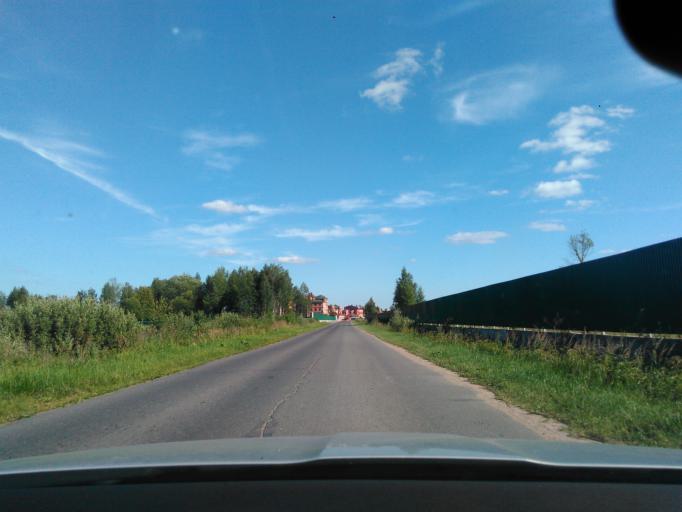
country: RU
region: Tverskaya
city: Konakovo
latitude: 56.6794
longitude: 36.7073
